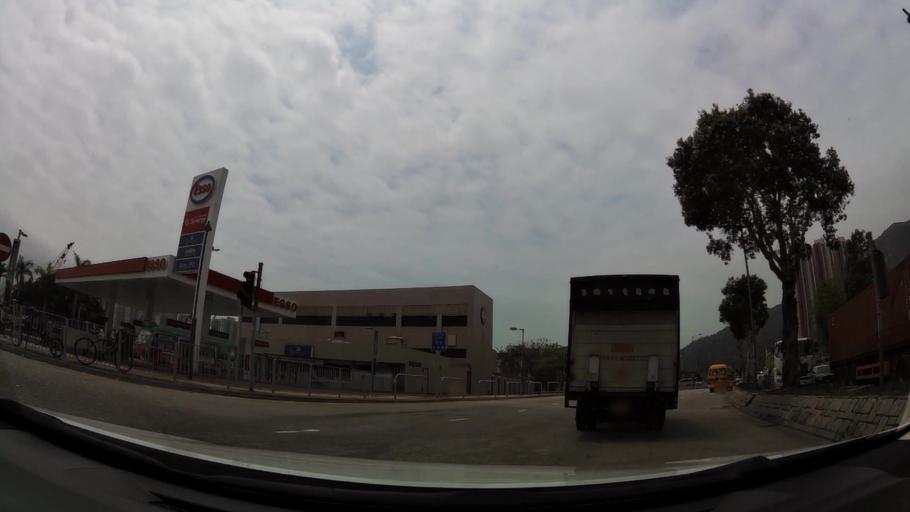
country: HK
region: Tuen Mun
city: Tuen Mun
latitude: 22.3806
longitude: 113.9712
